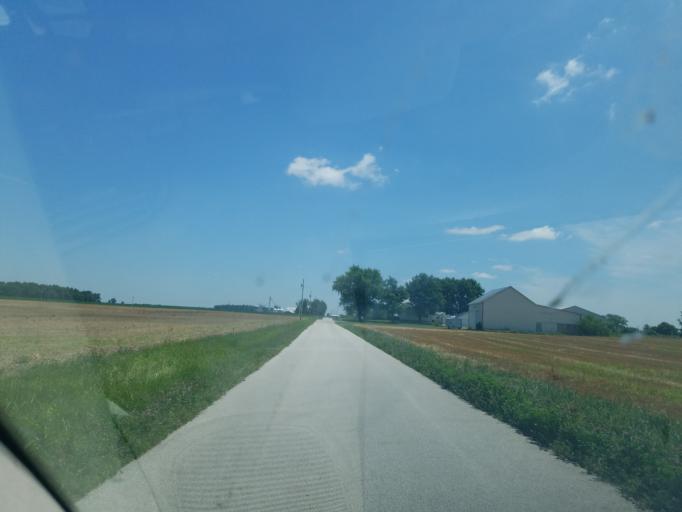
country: US
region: Ohio
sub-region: Hancock County
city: Arlington
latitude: 40.8483
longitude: -83.6043
